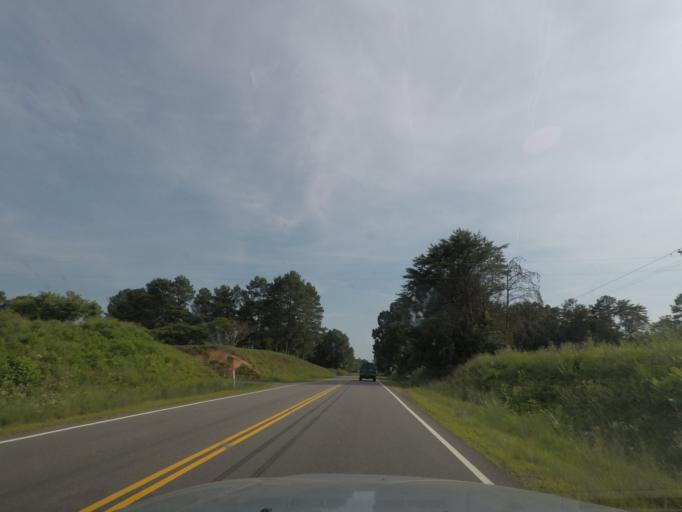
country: US
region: Virginia
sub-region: Mecklenburg County
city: Chase City
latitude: 36.8132
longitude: -78.5995
